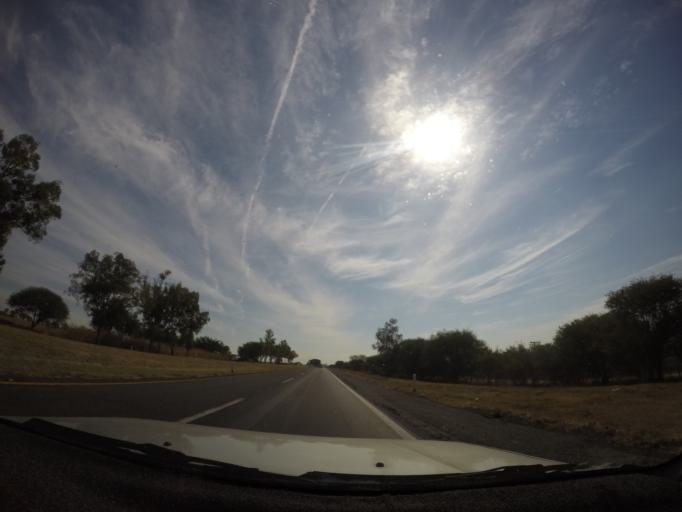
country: MX
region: Jalisco
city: La Barca
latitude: 20.3219
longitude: -102.5251
